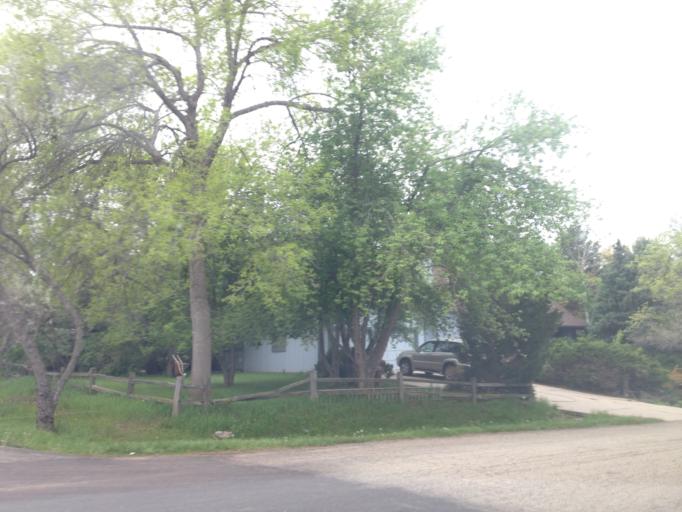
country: US
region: Colorado
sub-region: Boulder County
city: Louisville
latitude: 40.0068
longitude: -105.1711
